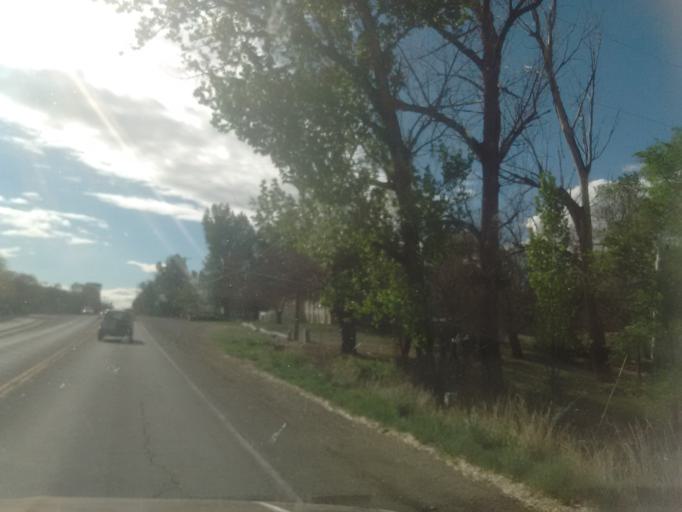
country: US
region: Colorado
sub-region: Mesa County
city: Redlands
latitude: 39.0848
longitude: -108.6471
